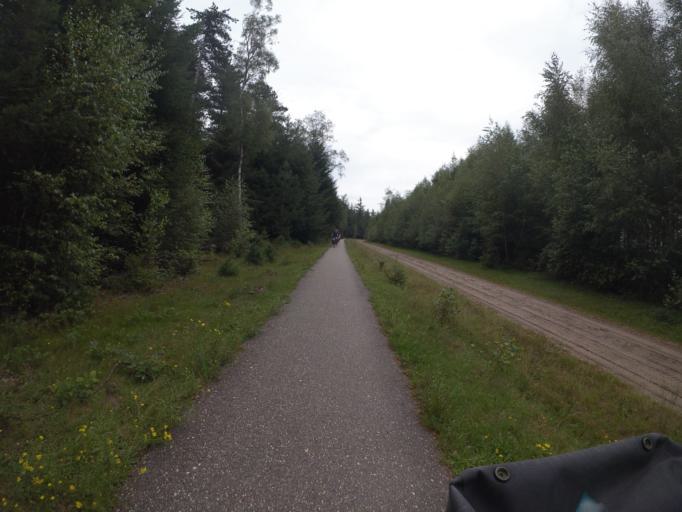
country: NL
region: North Brabant
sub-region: Gemeente Valkenswaard
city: Valkenswaard
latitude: 51.3325
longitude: 5.4931
